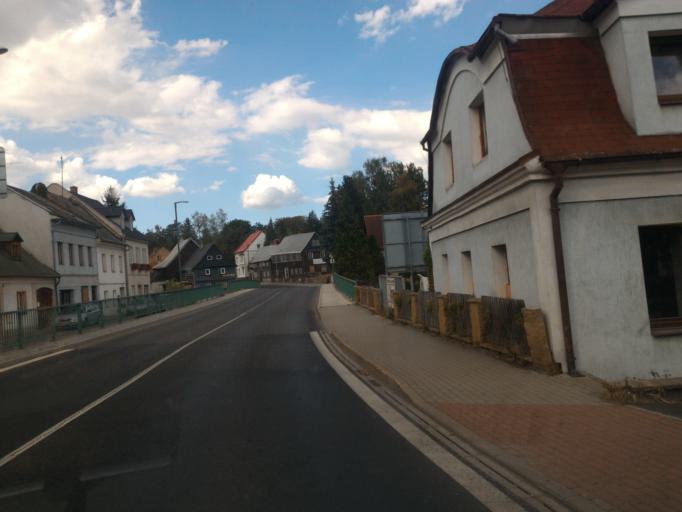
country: CZ
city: Mimon
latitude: 50.6608
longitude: 14.7246
